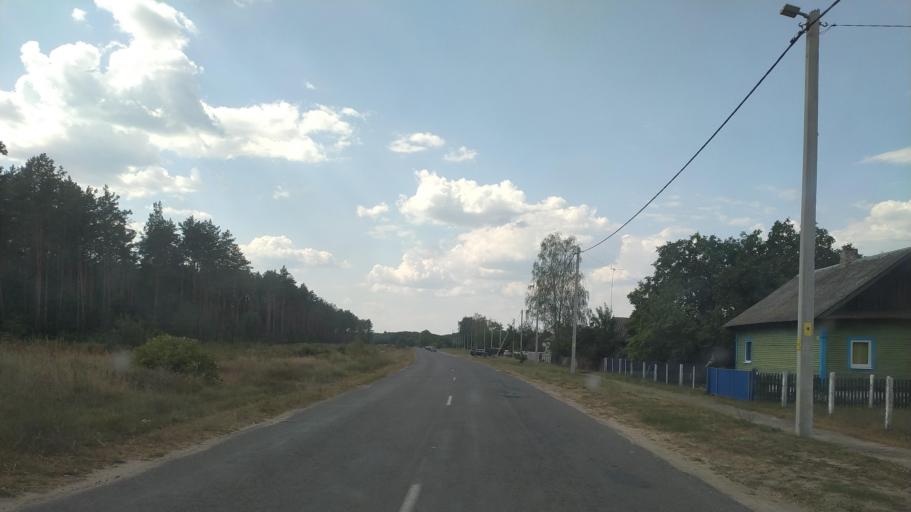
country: BY
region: Brest
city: Drahichyn
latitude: 52.1026
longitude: 25.1398
